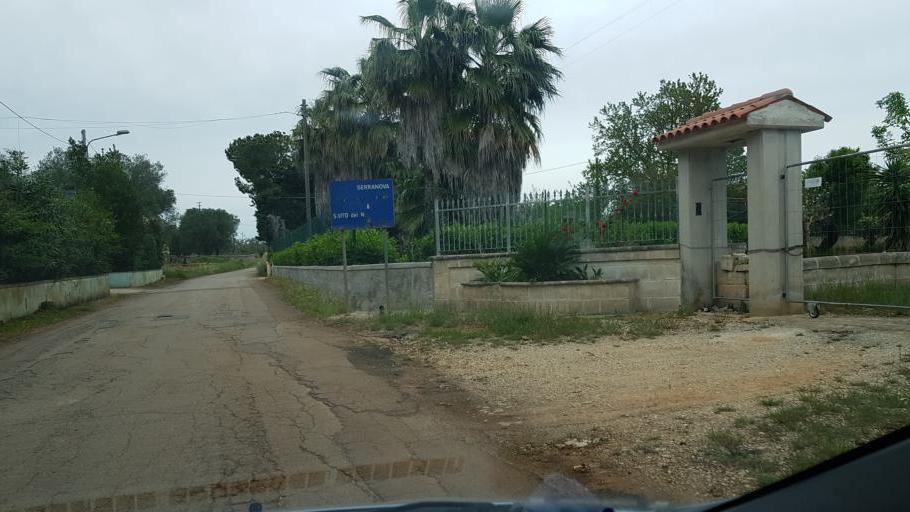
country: IT
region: Apulia
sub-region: Provincia di Brindisi
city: San Vito dei Normanni
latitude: 40.6640
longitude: 17.7292
